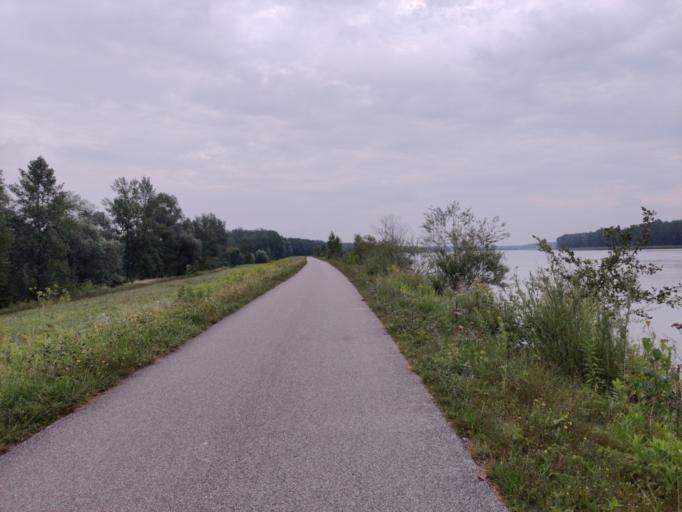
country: AT
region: Upper Austria
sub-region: Politischer Bezirk Linz-Land
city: Asten
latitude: 48.2579
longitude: 14.4073
